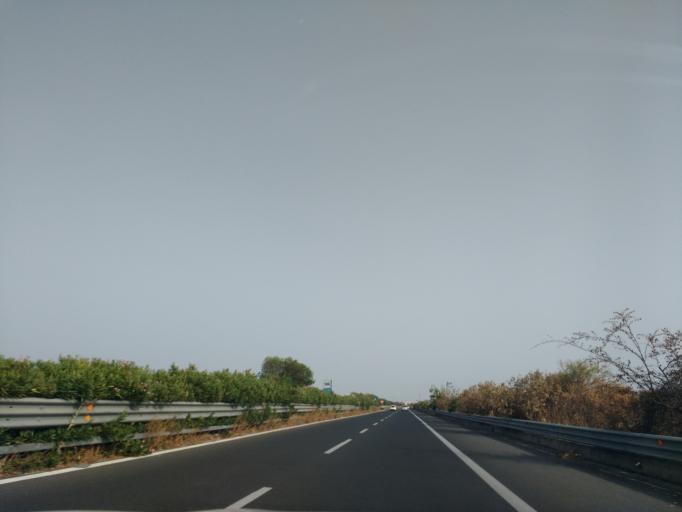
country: IT
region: Sicily
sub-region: Provincia di Siracusa
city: Citta Giardino
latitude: 37.1210
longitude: 15.1896
